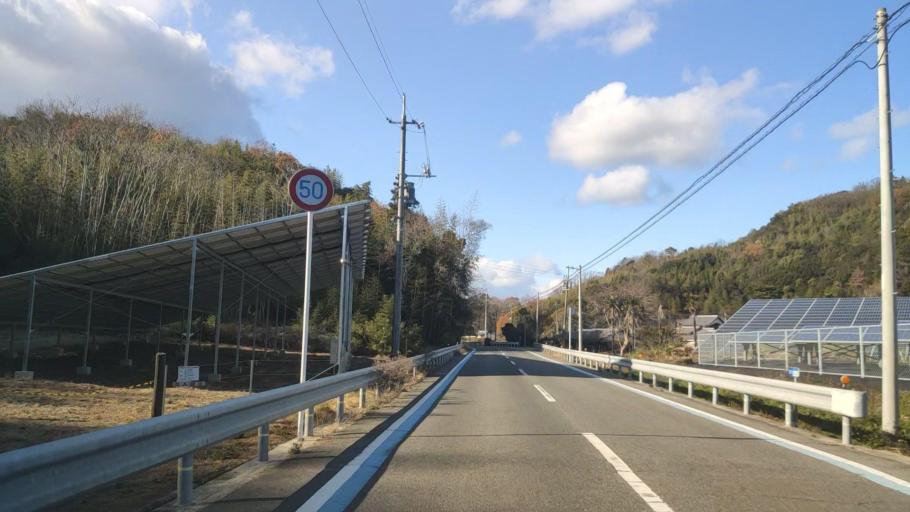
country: JP
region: Hiroshima
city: Innoshima
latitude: 34.2296
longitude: 133.1067
